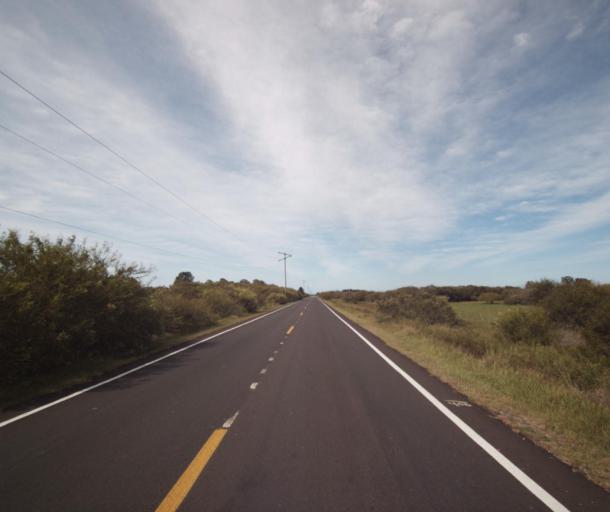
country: BR
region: Rio Grande do Sul
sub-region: Rio Grande
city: Rio Grande
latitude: -31.9153
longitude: -51.9409
